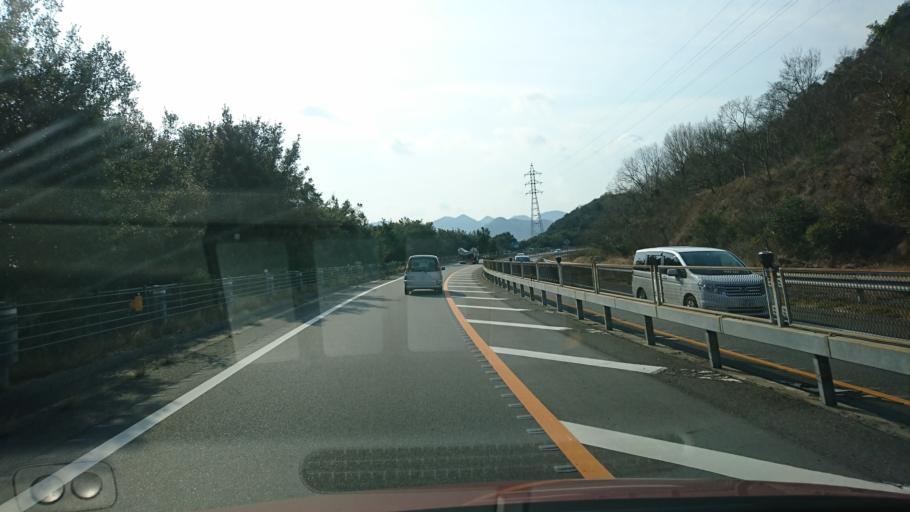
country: JP
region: Hiroshima
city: Onomichi
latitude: 34.3636
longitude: 133.1920
